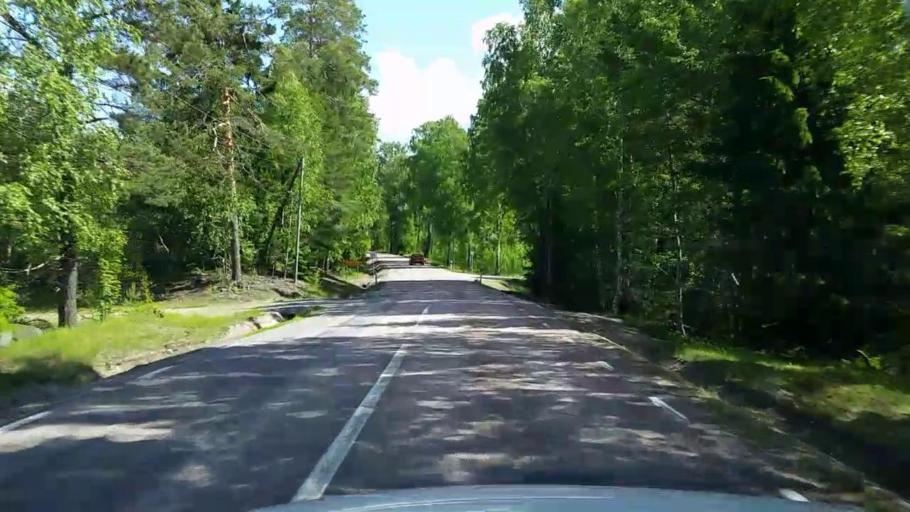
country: SE
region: Vaestmanland
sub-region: Kopings Kommun
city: Kolsva
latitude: 59.6976
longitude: 15.7821
